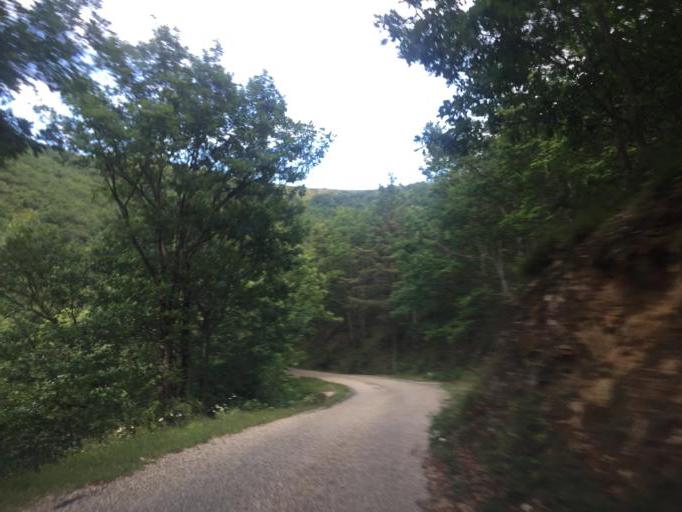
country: FR
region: Rhone-Alpes
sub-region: Departement de l'Ardeche
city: Flaviac
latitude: 44.7888
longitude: 4.6542
